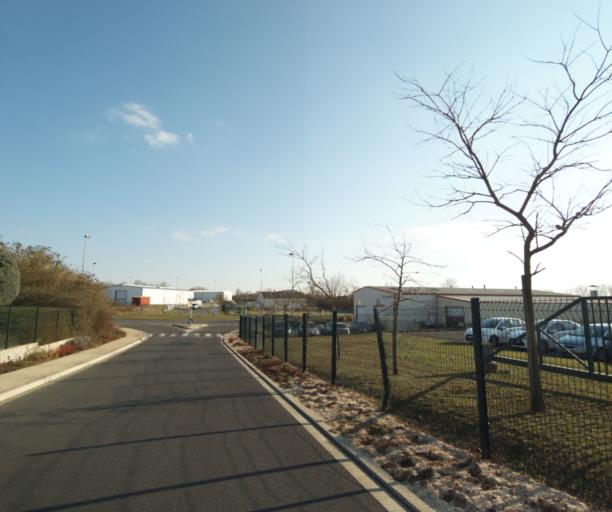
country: FR
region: Poitou-Charentes
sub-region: Departement des Deux-Sevres
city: Aiffres
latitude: 46.3302
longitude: -0.4163
